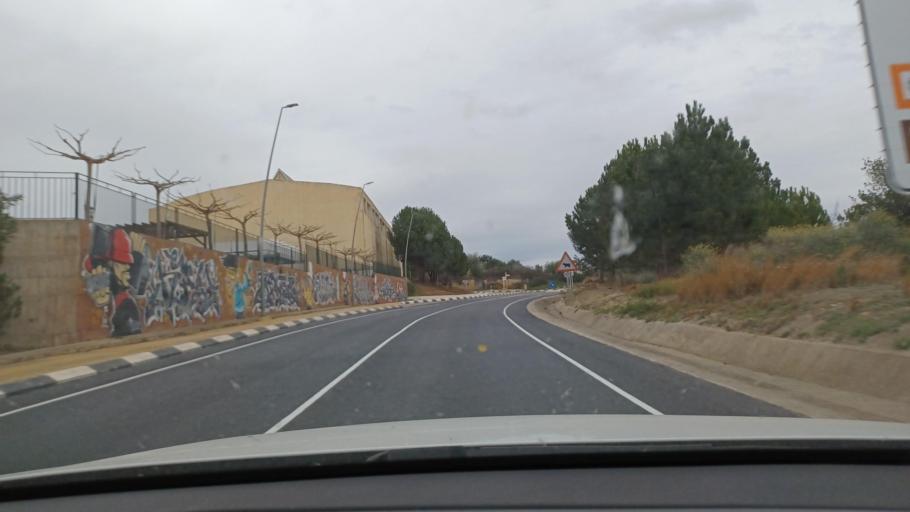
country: ES
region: Valencia
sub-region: Provincia de Castello
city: Traiguera
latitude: 40.5275
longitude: 0.2942
